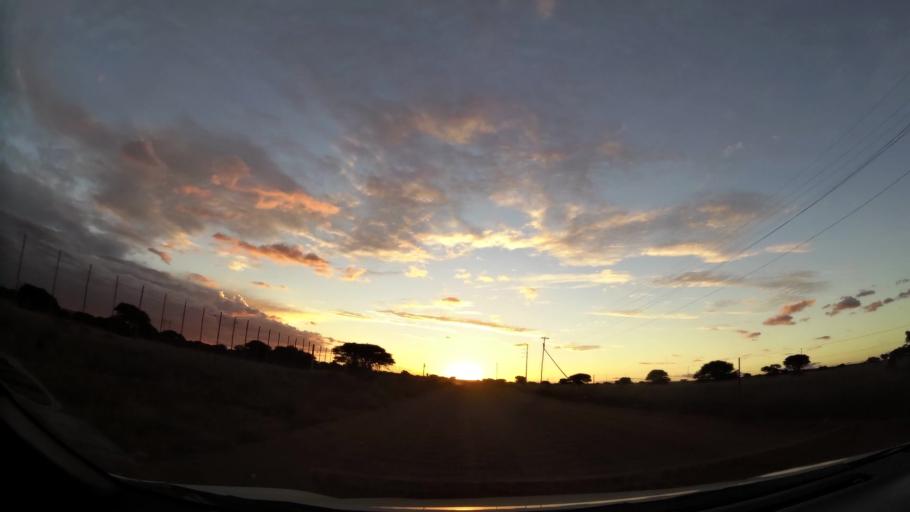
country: ZA
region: Limpopo
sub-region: Capricorn District Municipality
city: Polokwane
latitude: -23.7417
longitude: 29.4551
